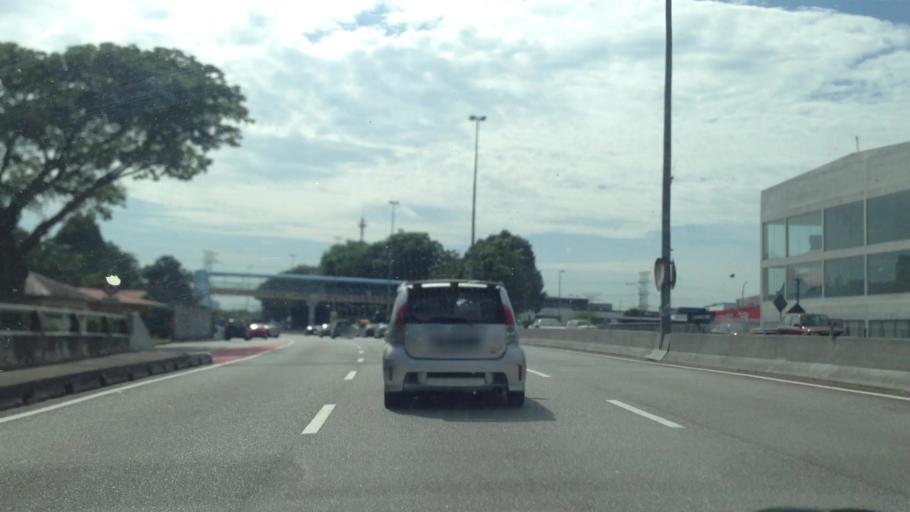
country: MY
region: Selangor
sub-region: Petaling
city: Petaling Jaya
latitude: 3.0747
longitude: 101.6165
